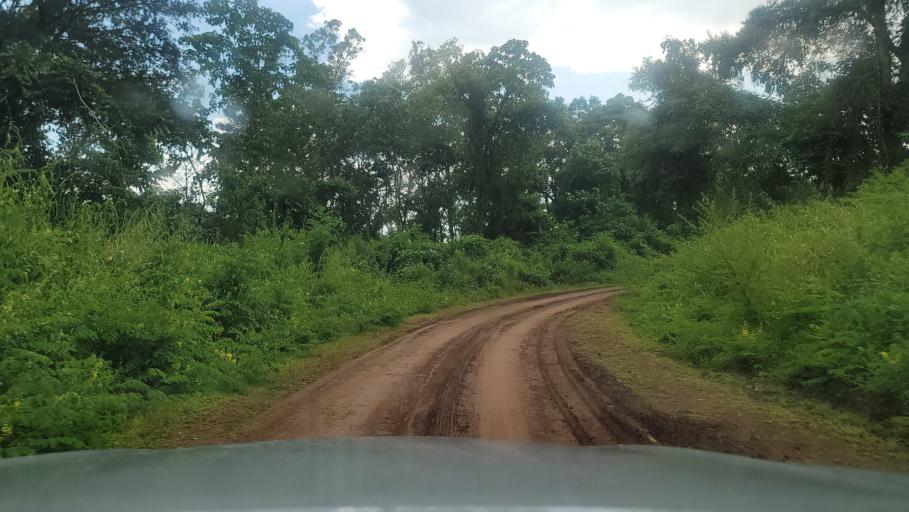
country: ET
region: Southern Nations, Nationalities, and People's Region
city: Bonga
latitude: 7.6389
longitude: 36.2342
